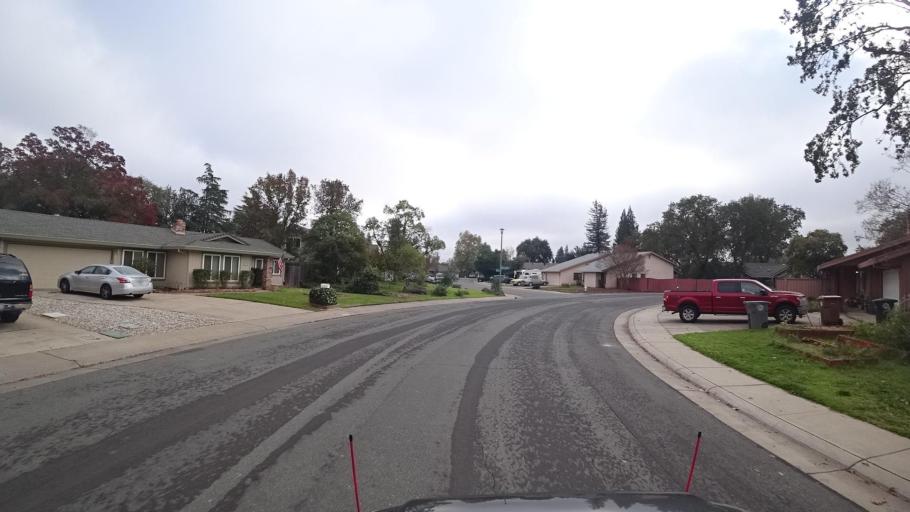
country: US
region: California
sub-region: Sacramento County
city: Elk Grove
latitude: 38.4115
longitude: -121.3661
